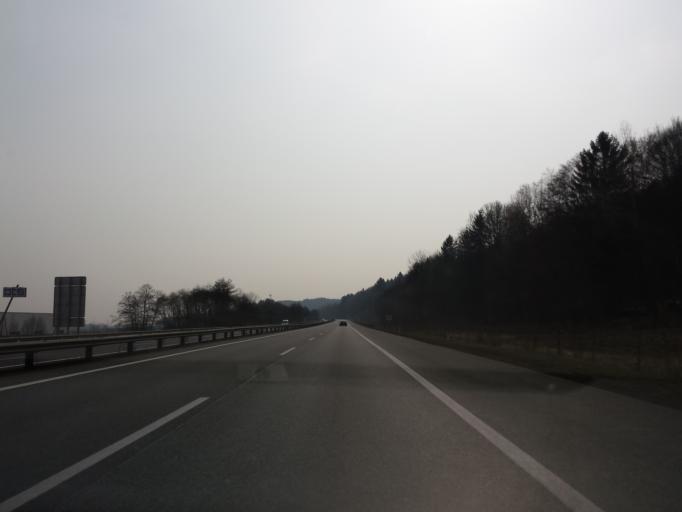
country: AT
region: Styria
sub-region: Politischer Bezirk Weiz
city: Sinabelkirchen
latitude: 47.0952
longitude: 15.8266
